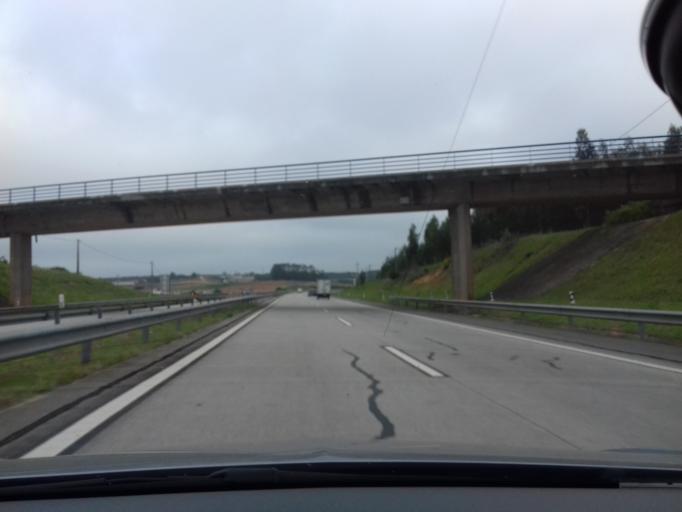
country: PT
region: Leiria
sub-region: Bombarral
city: Bombarral
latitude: 39.1852
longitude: -9.2056
